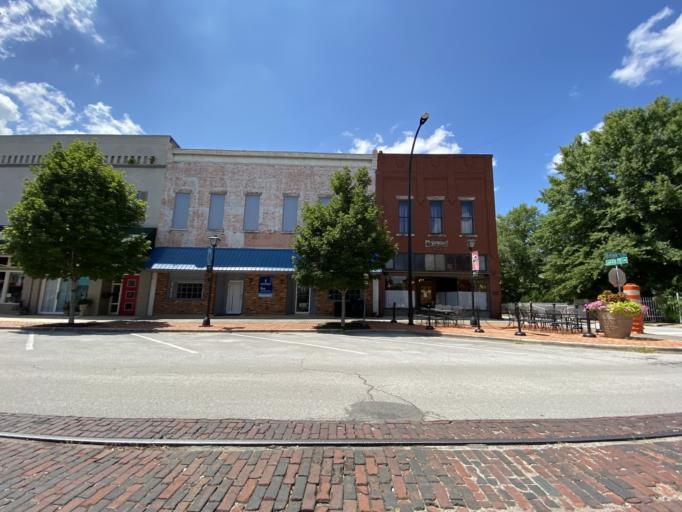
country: US
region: Alabama
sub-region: Morgan County
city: Decatur
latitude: 34.6128
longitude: -86.9849
